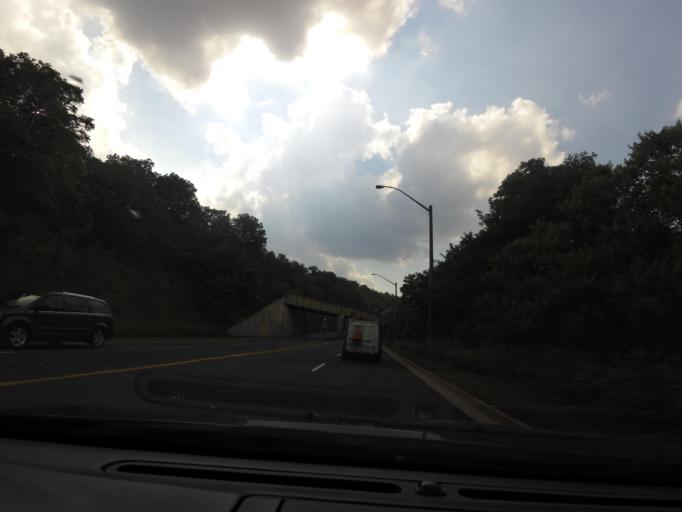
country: CA
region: Ontario
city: Hamilton
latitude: 43.2340
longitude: -79.8247
